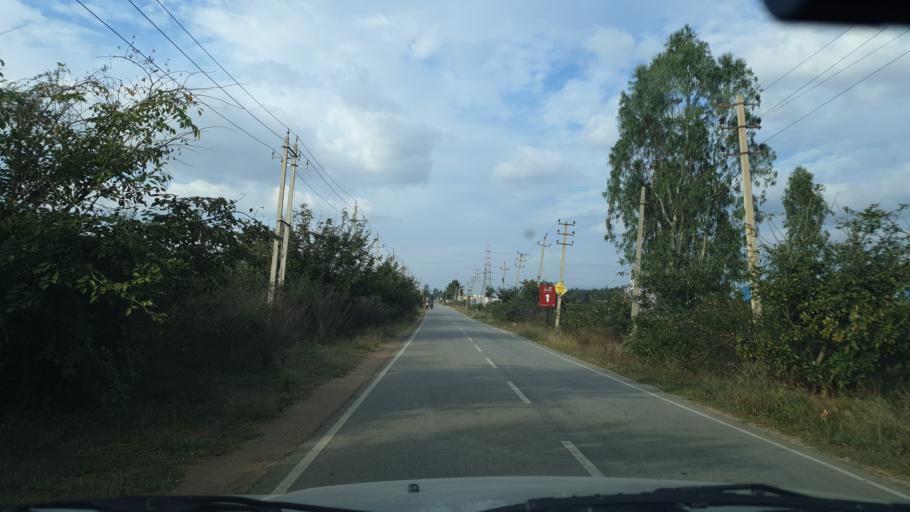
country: IN
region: Karnataka
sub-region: Bangalore Urban
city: Yelahanka
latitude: 13.1937
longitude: 77.6014
